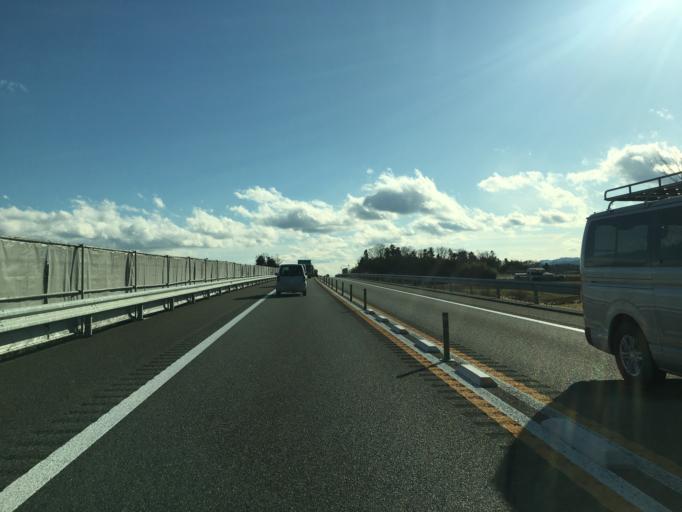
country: JP
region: Fukushima
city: Namie
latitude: 37.5696
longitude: 140.9438
